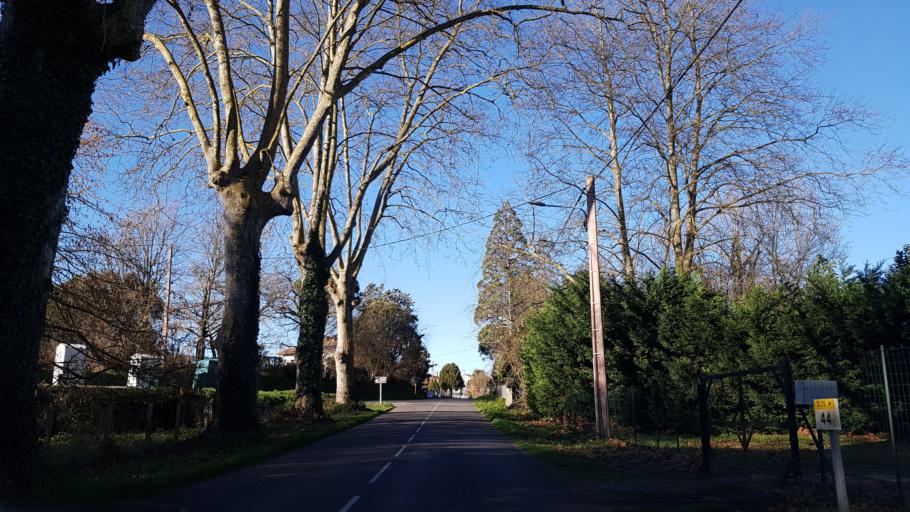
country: FR
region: Midi-Pyrenees
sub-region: Departement de la Haute-Garonne
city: Calmont
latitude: 43.2873
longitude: 1.6239
